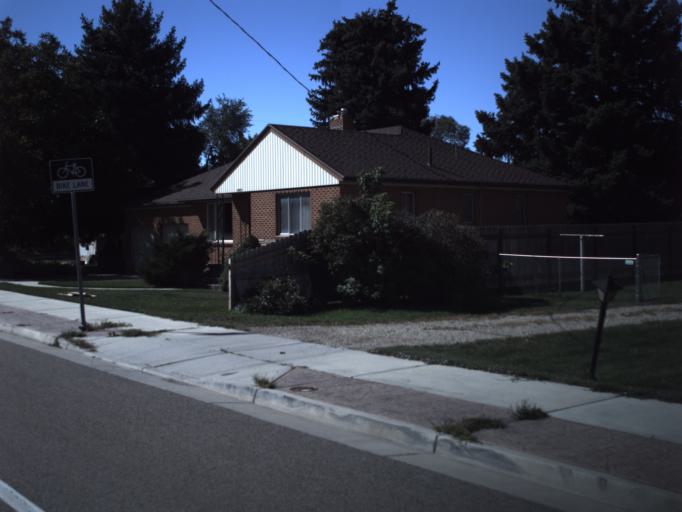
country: US
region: Utah
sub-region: Salt Lake County
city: Bluffdale
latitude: 40.4939
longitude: -111.9389
